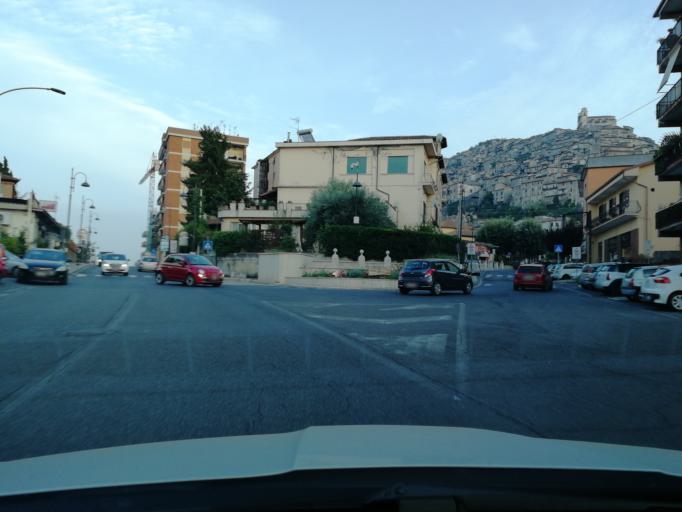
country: IT
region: Latium
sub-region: Citta metropolitana di Roma Capitale
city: Artena
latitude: 41.7425
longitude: 12.9114
